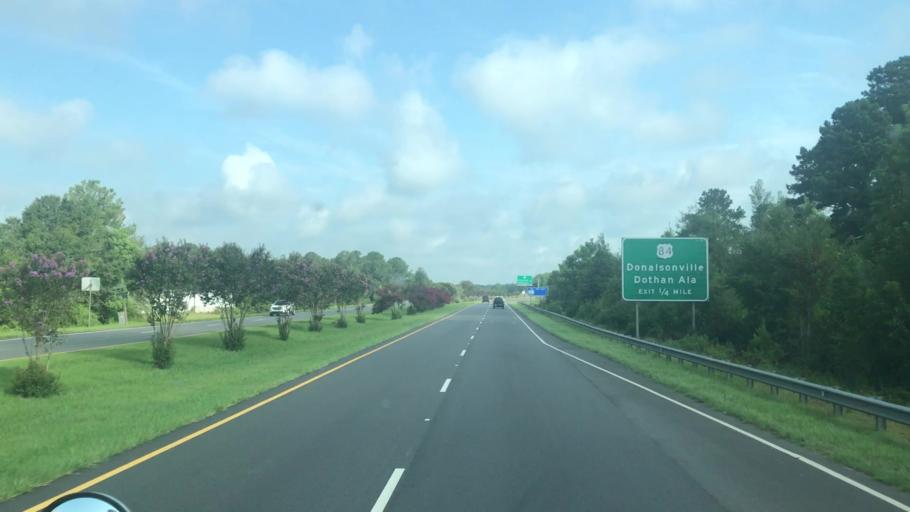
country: US
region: Georgia
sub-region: Decatur County
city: Bainbridge
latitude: 30.9145
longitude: -84.5973
